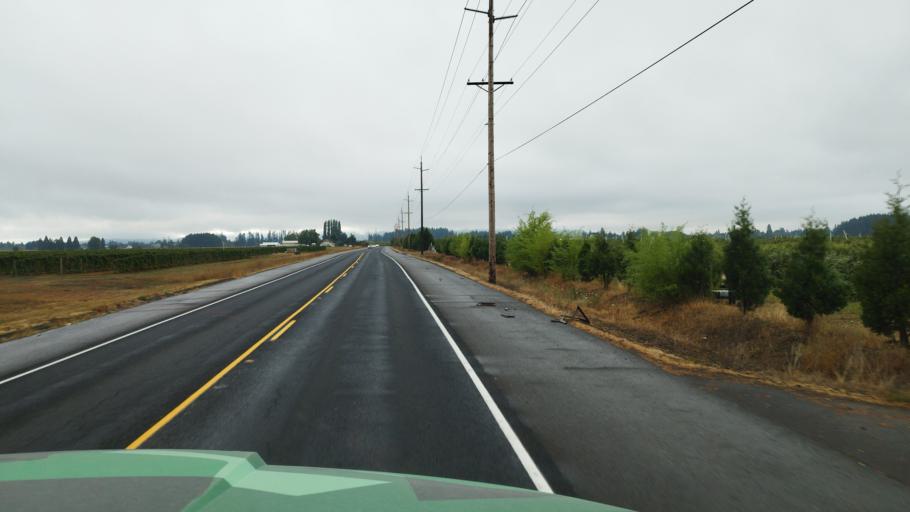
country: US
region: Oregon
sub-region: Washington County
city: Cornelius
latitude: 45.5473
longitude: -123.0735
